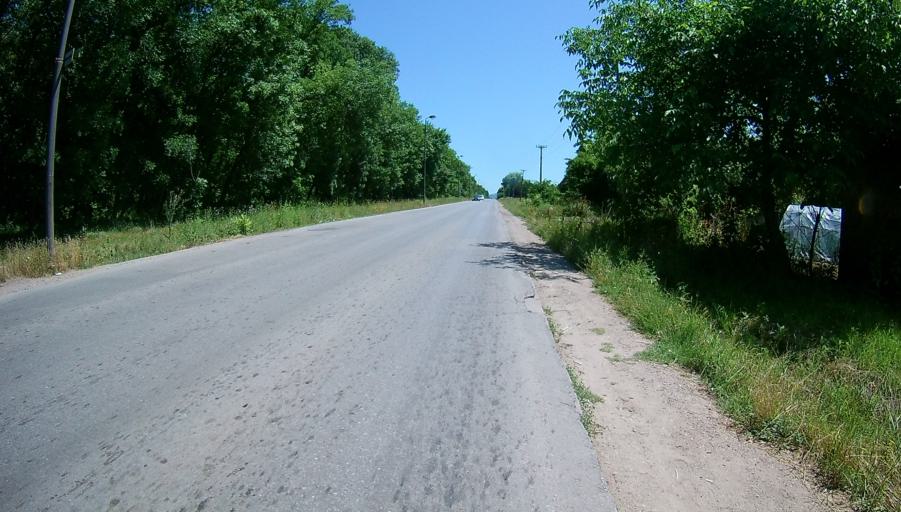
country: RS
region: Central Serbia
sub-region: Nisavski Okrug
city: Nis
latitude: 43.3049
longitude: 21.8679
